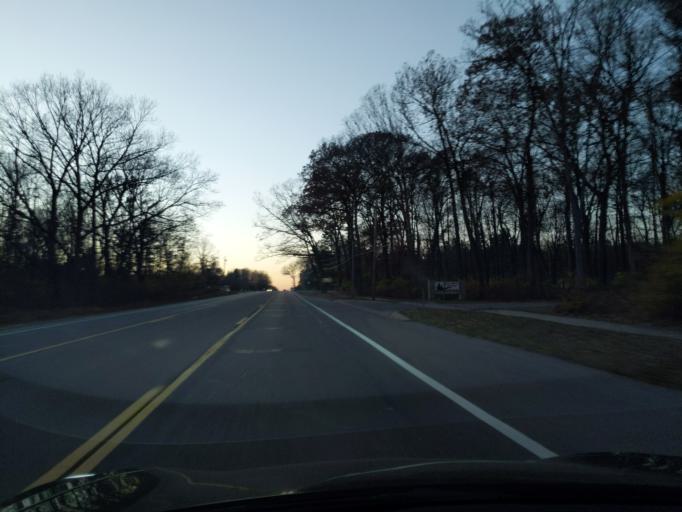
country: US
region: Michigan
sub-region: Ingham County
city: Haslett
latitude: 42.7114
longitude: -84.3734
